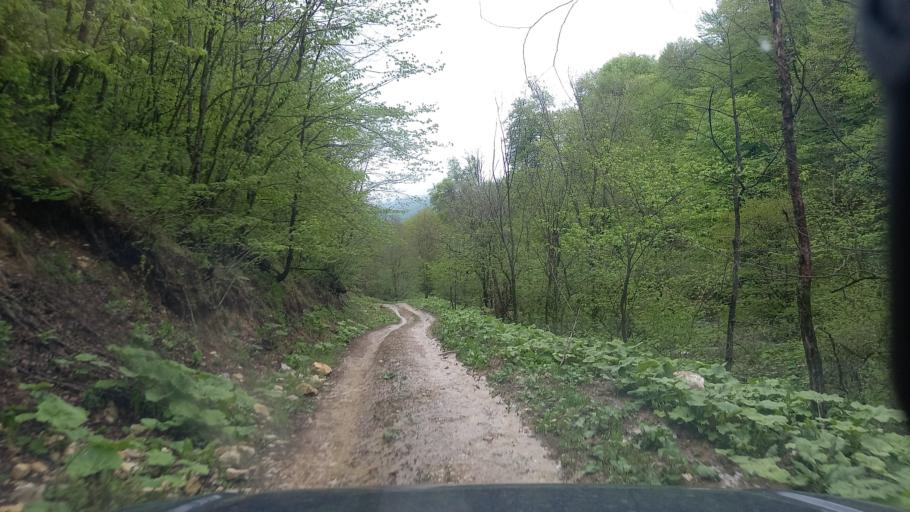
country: RU
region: Kabardino-Balkariya
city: Babugent
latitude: 43.2139
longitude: 43.5472
